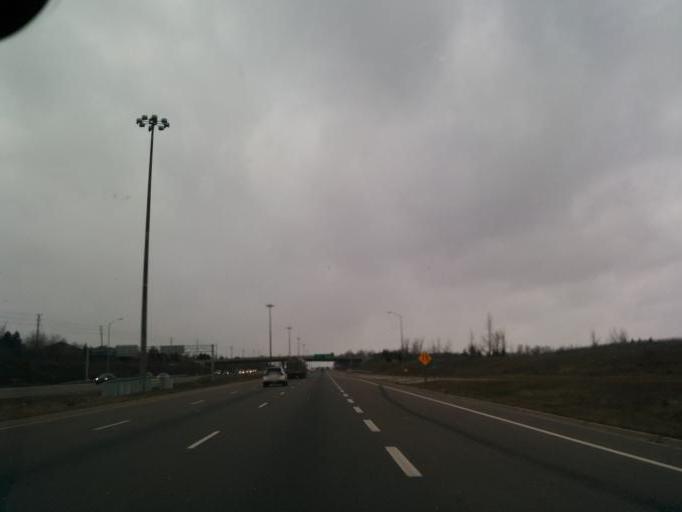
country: CA
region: Ontario
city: Brampton
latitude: 43.7168
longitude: -79.7532
